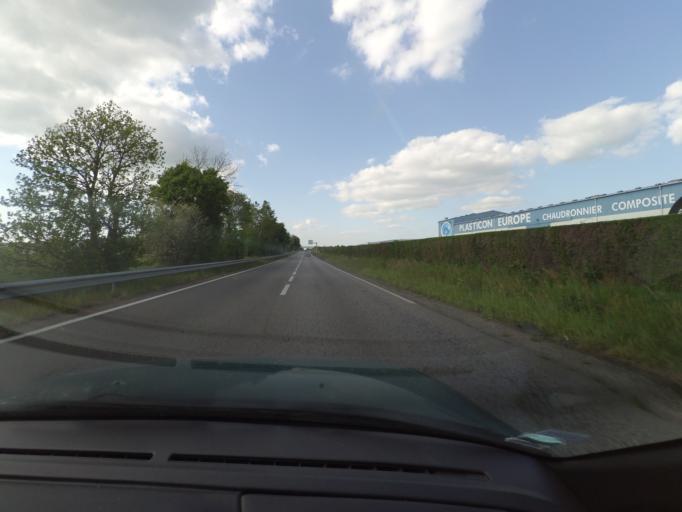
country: FR
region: Pays de la Loire
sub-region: Departement de la Vendee
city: Mouilleron-le-Captif
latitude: 46.7407
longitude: -1.4302
